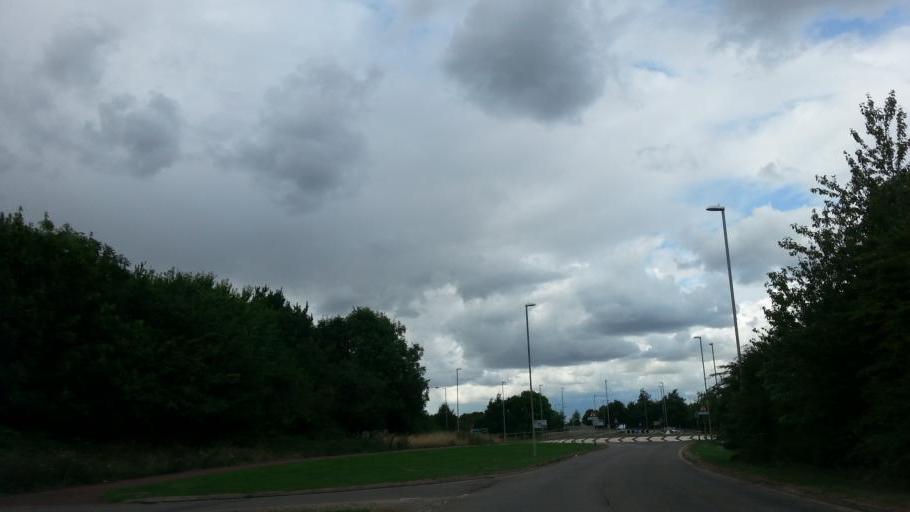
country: GB
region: England
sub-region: Cambridgeshire
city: Papworth Everard
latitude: 52.2230
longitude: -0.0723
